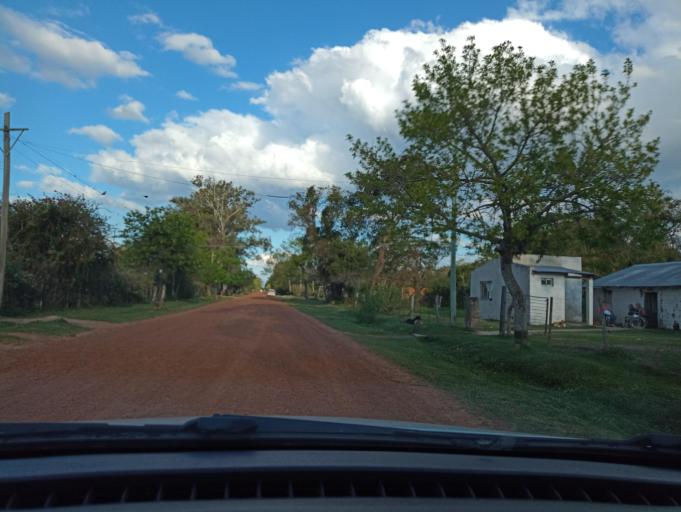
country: AR
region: Corrientes
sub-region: Departamento de San Miguel
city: San Miguel
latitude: -28.5355
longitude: -57.1753
